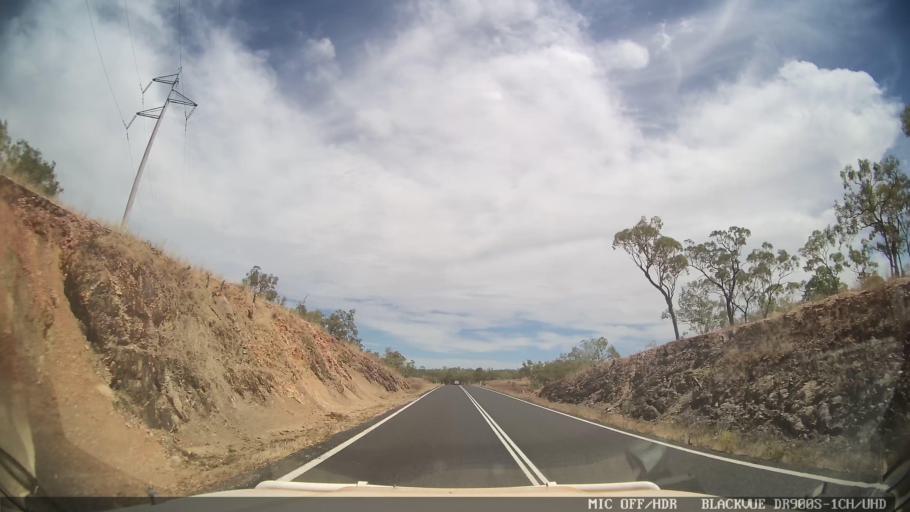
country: AU
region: Queensland
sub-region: Cairns
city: Port Douglas
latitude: -16.1409
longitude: 144.7715
